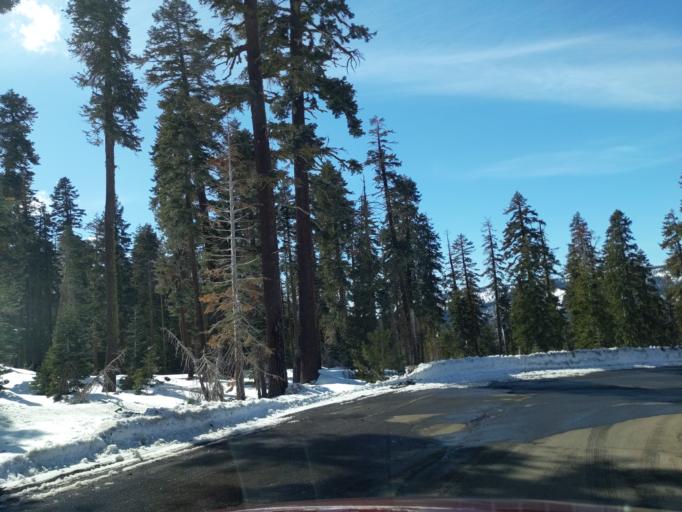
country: US
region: California
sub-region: El Dorado County
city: South Lake Tahoe
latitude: 38.8016
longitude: -120.0844
